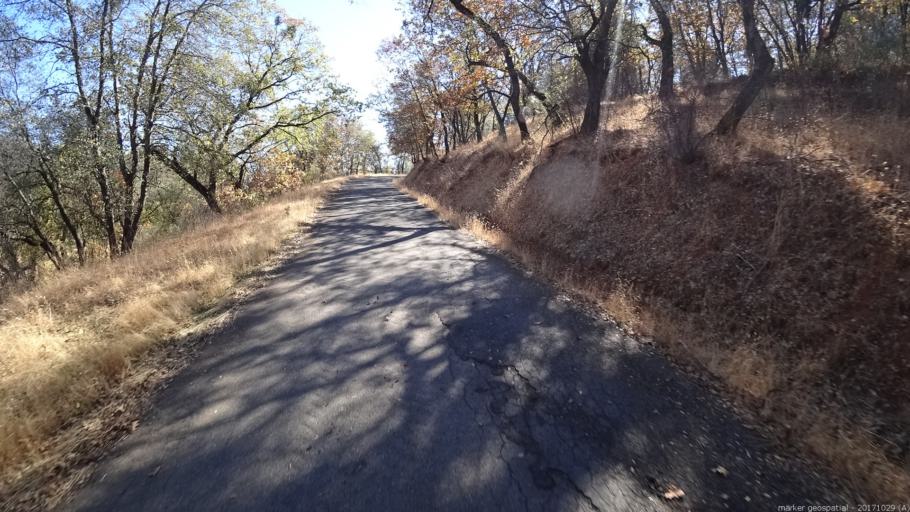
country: US
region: California
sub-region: Shasta County
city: Shasta
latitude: 40.4738
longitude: -122.6827
